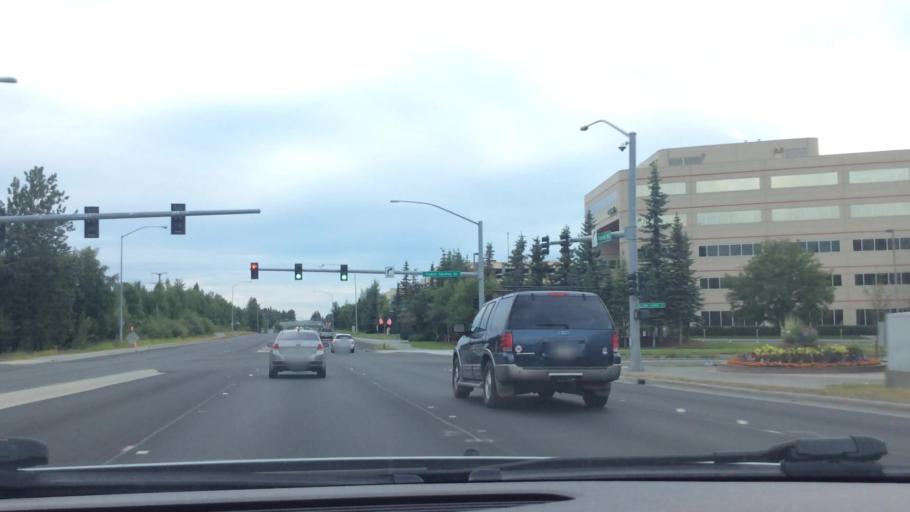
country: US
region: Alaska
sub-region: Anchorage Municipality
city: Anchorage
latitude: 61.1808
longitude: -149.7944
